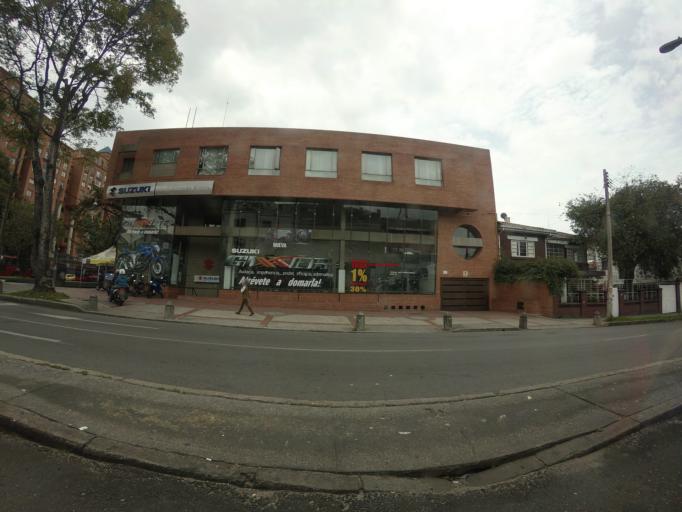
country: CO
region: Bogota D.C.
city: Bogota
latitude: 4.6205
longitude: -74.0705
